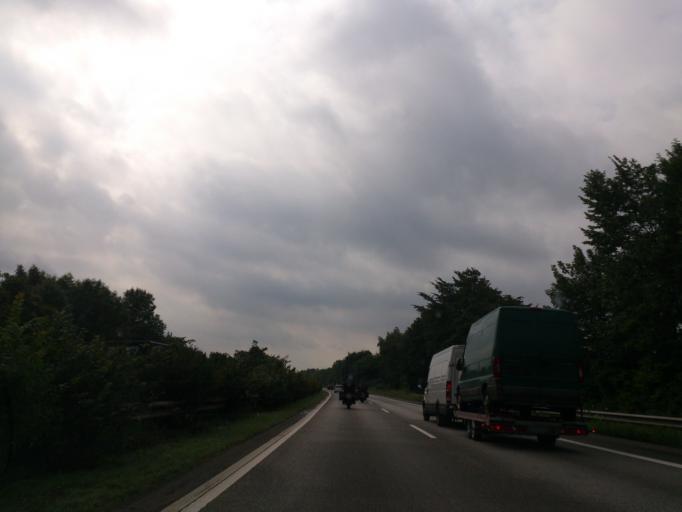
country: DE
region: Schleswig-Holstein
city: Seeth-Ekholt
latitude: 53.7365
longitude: 9.7178
